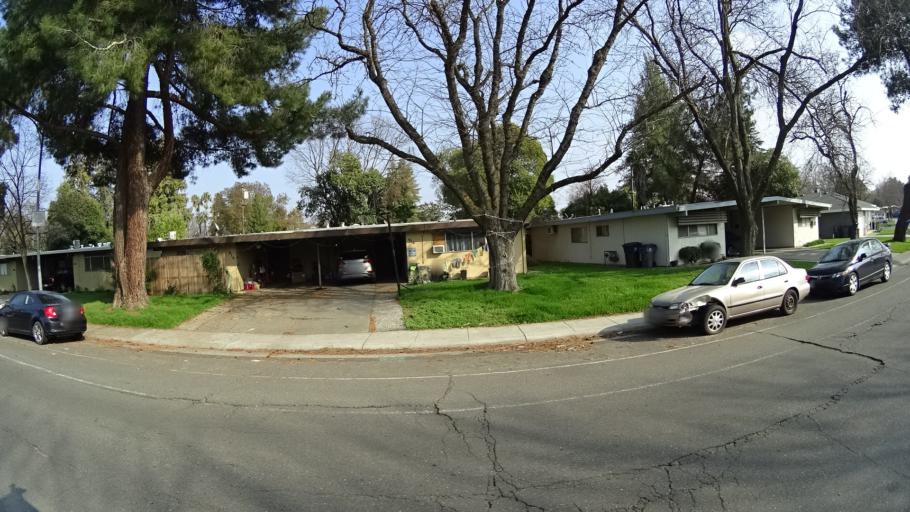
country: US
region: California
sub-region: Yolo County
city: Davis
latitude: 38.5533
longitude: -121.7395
